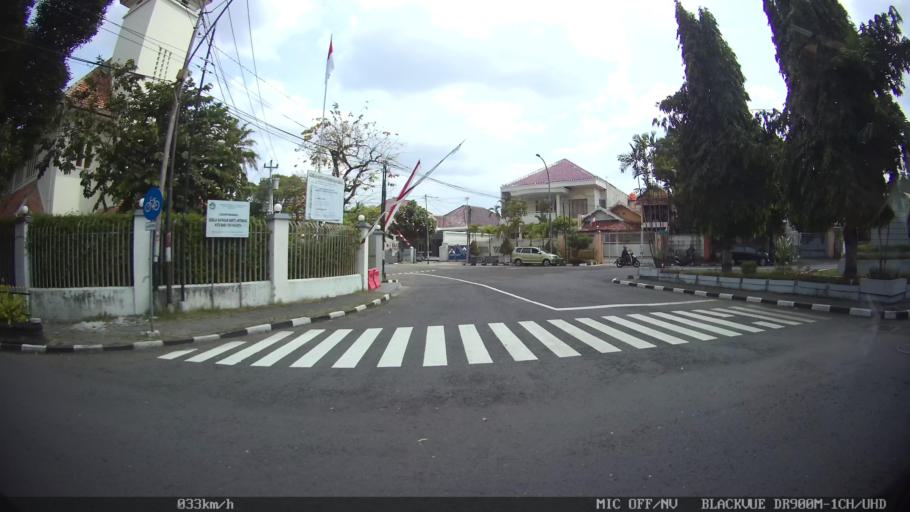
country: ID
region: Daerah Istimewa Yogyakarta
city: Yogyakarta
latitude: -7.7885
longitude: 110.3708
